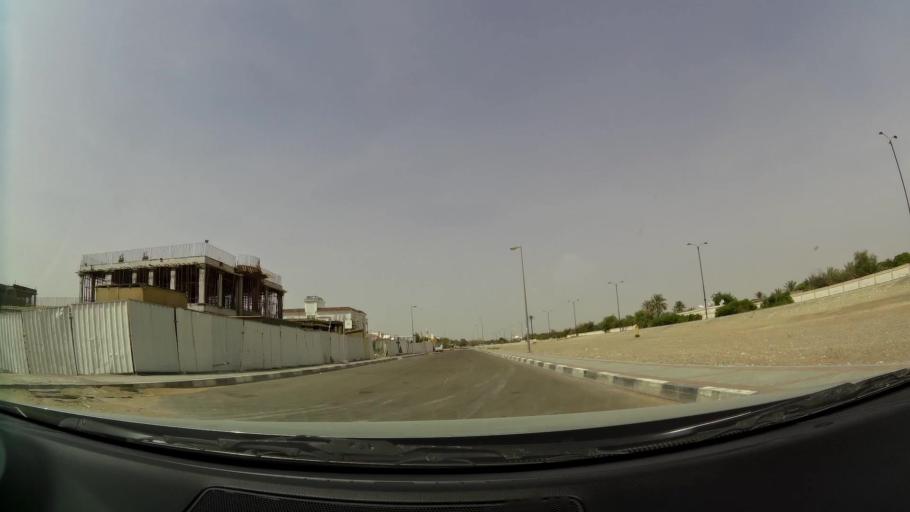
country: AE
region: Abu Dhabi
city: Al Ain
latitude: 24.1583
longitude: 55.6654
